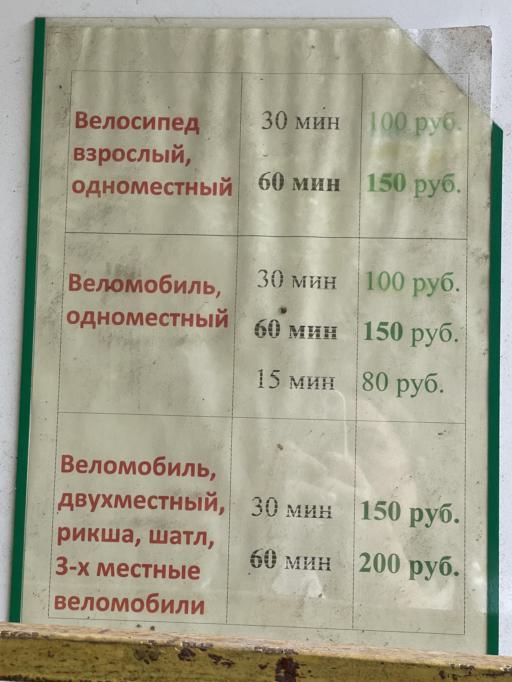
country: RU
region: Chuvashia
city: Novocheboksarsk
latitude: 56.1192
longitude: 47.4769
